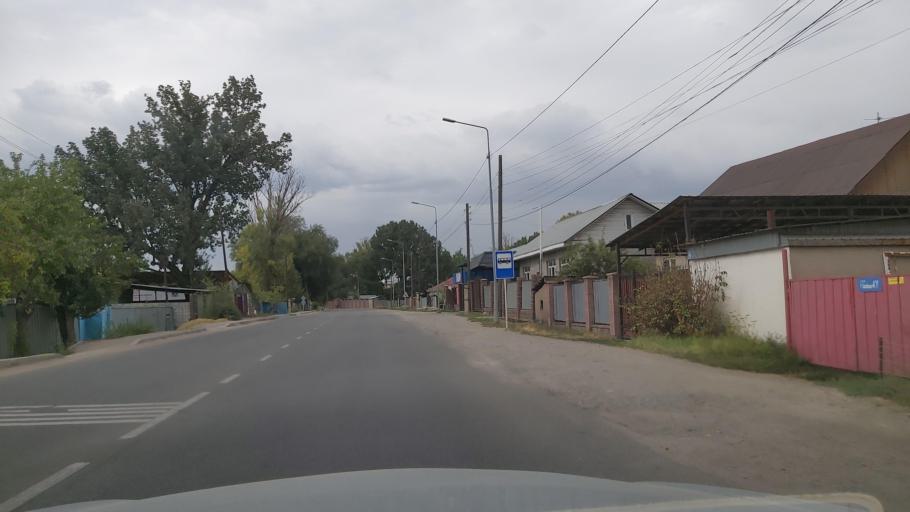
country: KZ
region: Almaty Oblysy
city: Energeticheskiy
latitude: 43.3857
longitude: 77.0781
